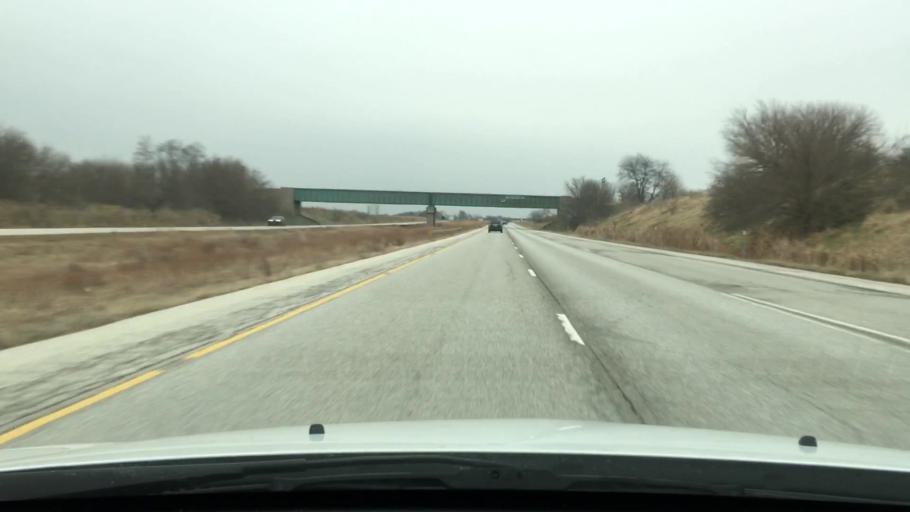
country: US
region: Illinois
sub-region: Morgan County
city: Jacksonville
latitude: 39.7266
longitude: -90.1641
